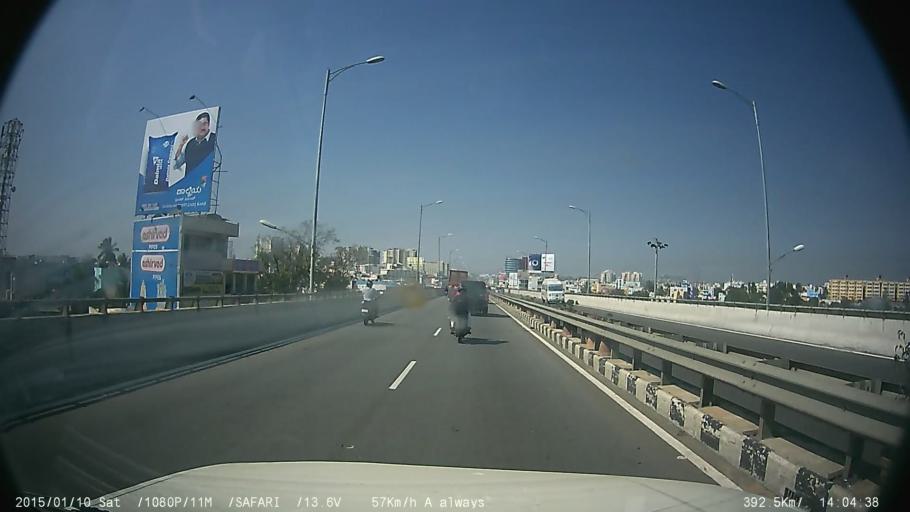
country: IN
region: Karnataka
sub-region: Bangalore Urban
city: Bangalore
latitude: 12.8934
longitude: 77.6373
